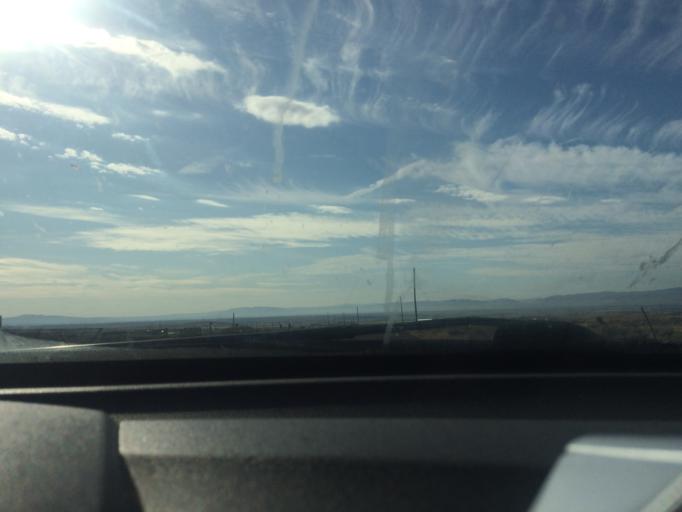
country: US
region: Washington
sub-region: Kittitas County
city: Ellensburg
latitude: 47.1558
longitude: -120.6315
